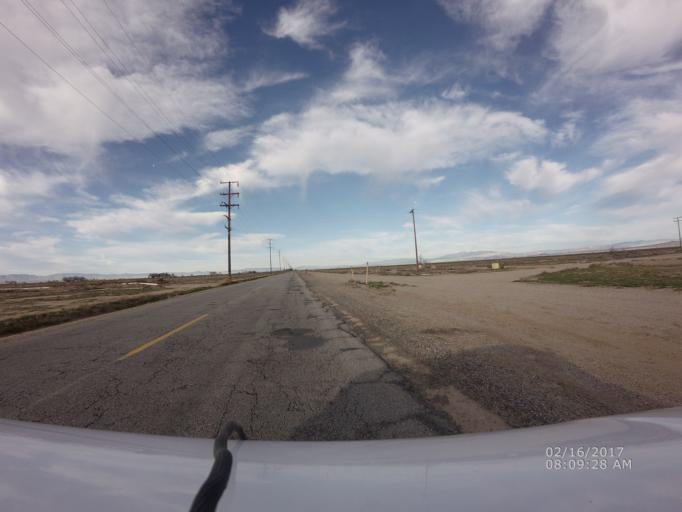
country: US
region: California
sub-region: Los Angeles County
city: Lancaster
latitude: 34.7636
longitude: -117.9959
